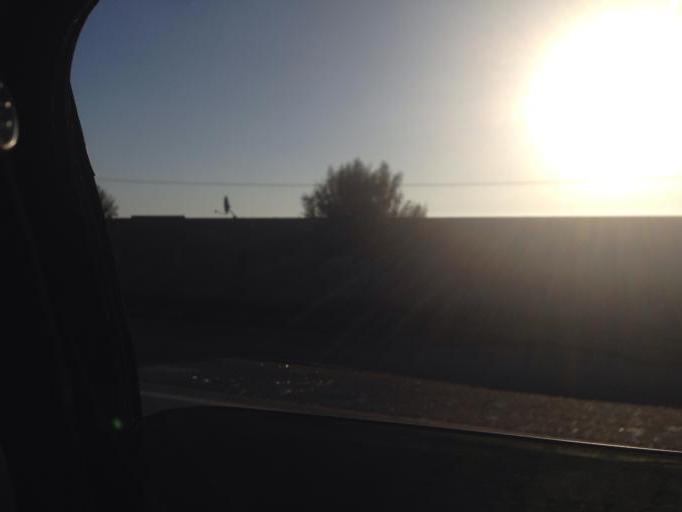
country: MX
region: Baja California
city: El Sauzal
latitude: 31.8738
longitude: -116.6793
